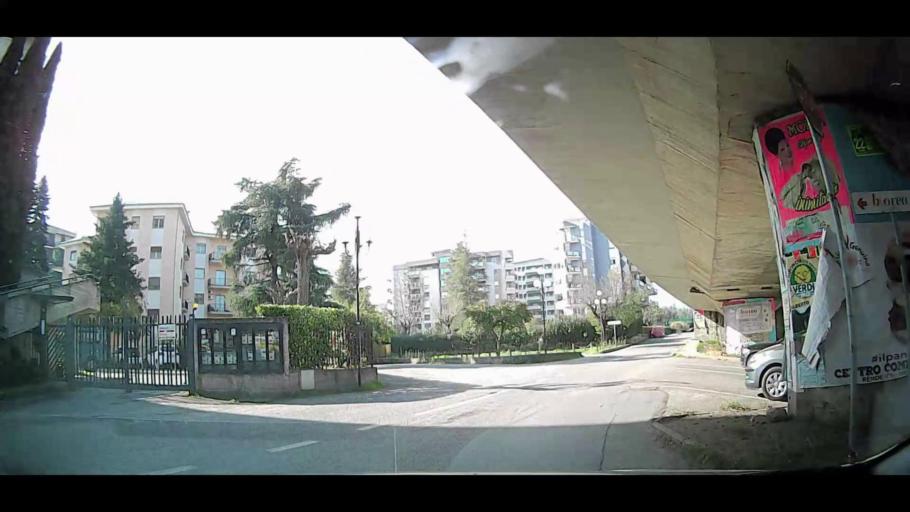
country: IT
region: Calabria
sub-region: Provincia di Cosenza
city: Quattromiglia
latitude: 39.3323
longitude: 16.2397
